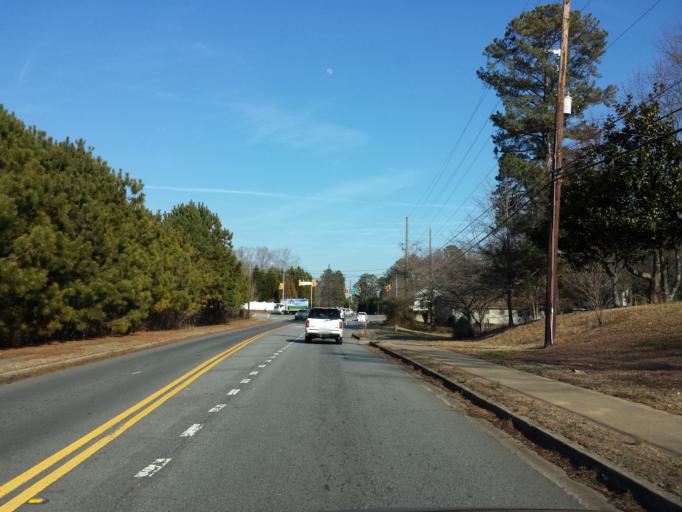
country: US
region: Georgia
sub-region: Cherokee County
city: Woodstock
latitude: 34.0394
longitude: -84.5109
